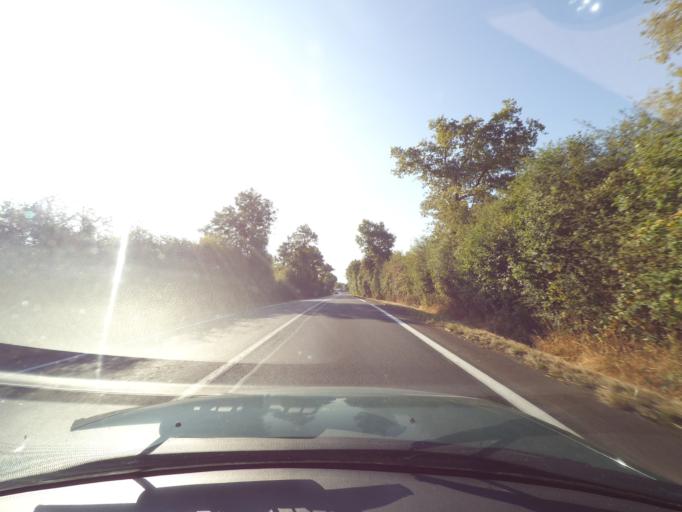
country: FR
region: Poitou-Charentes
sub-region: Departement des Deux-Sevres
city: Chiche
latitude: 46.8035
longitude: -0.3729
